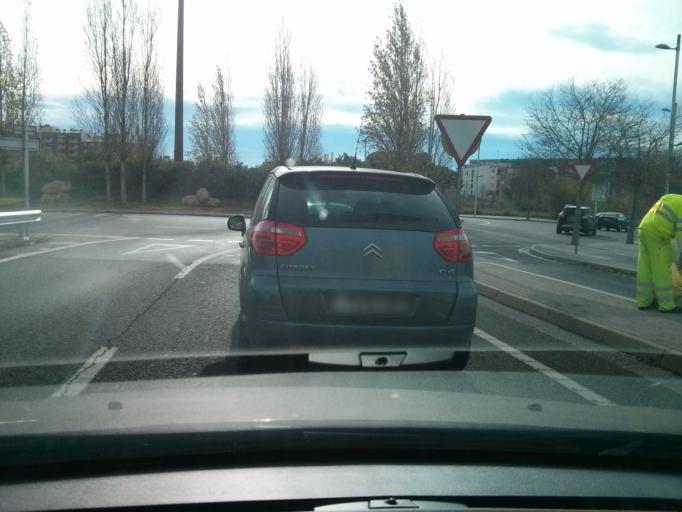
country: ES
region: Catalonia
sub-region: Provincia de Tarragona
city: Tarragona
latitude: 41.1252
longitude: 1.2426
